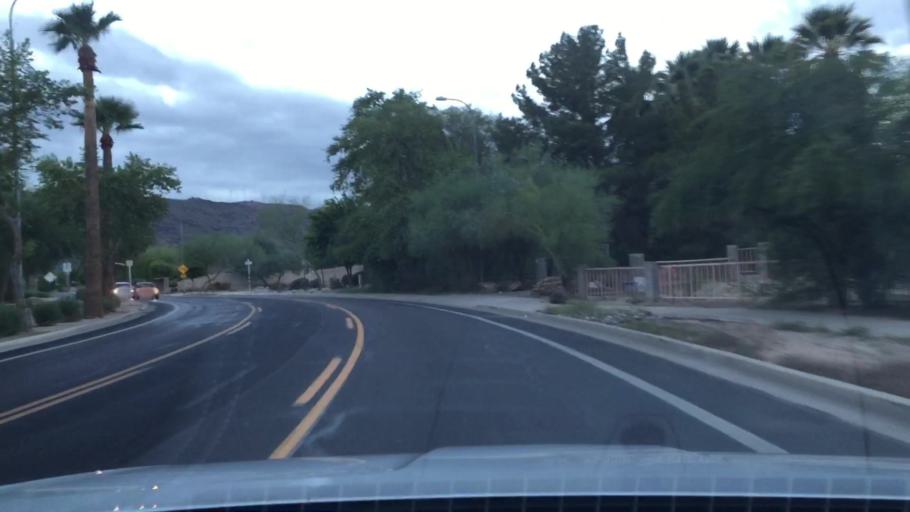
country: US
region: Arizona
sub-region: Maricopa County
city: Phoenix
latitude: 33.3750
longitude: -112.0487
